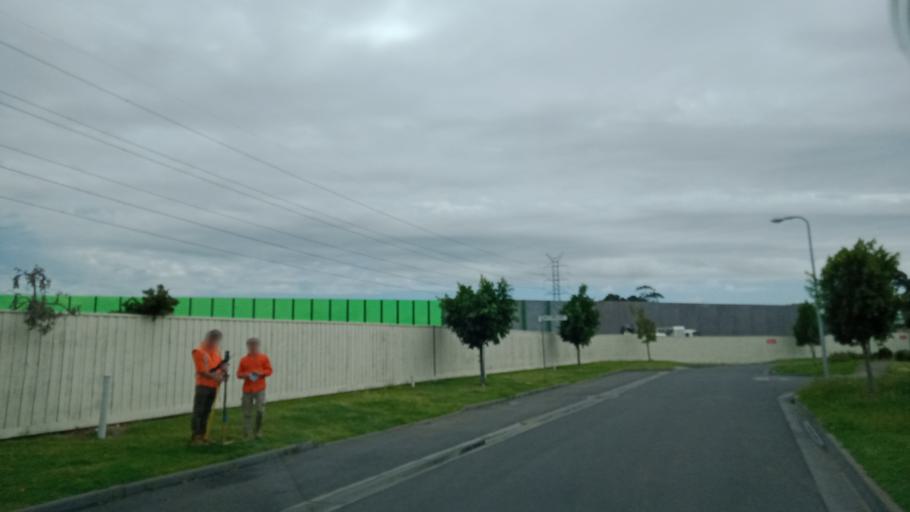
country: AU
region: Victoria
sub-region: Monash
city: Mulgrave
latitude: -37.9287
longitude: 145.1858
